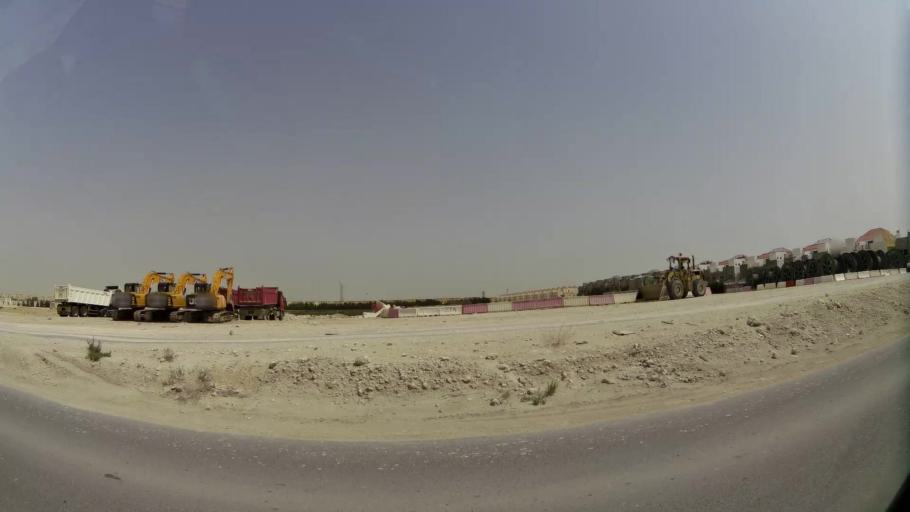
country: QA
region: Baladiyat ar Rayyan
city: Ar Rayyan
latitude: 25.2314
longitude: 51.4083
